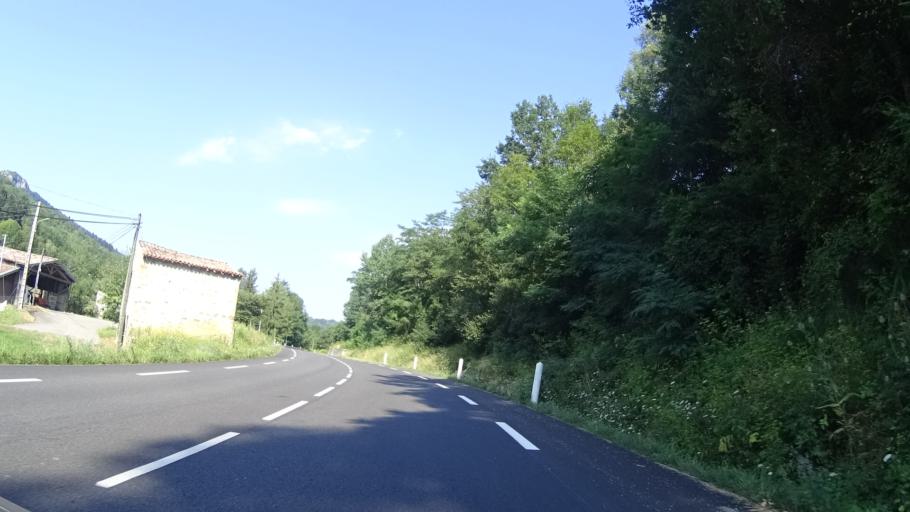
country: FR
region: Midi-Pyrenees
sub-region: Departement de l'Ariege
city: Lavelanet
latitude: 42.9136
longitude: 1.7746
